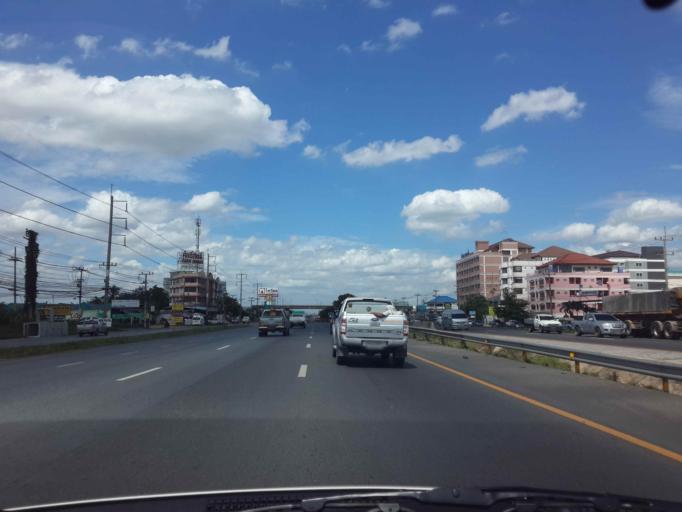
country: TH
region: Samut Sakhon
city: Samut Sakhon
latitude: 13.5757
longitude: 100.2990
